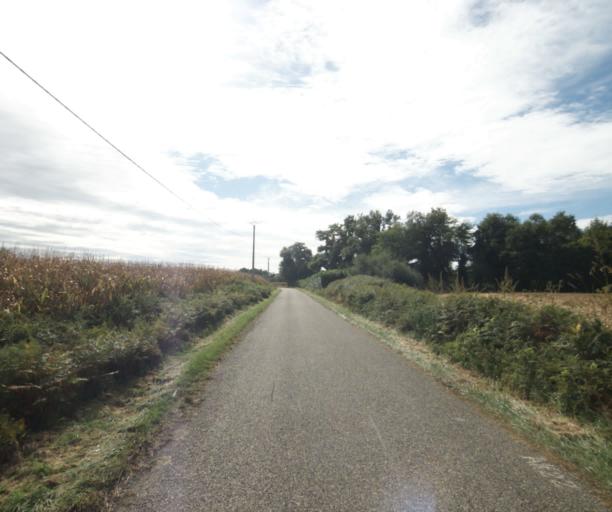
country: FR
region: Aquitaine
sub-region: Departement des Landes
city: Villeneuve-de-Marsan
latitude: 43.8991
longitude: -0.2274
